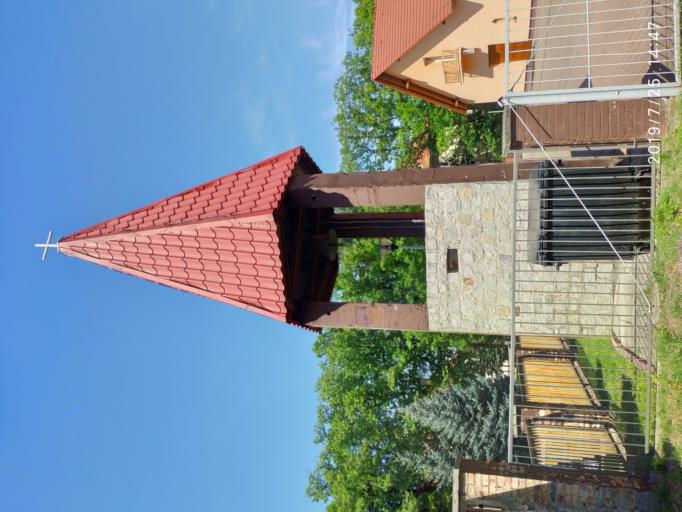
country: PL
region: Lubusz
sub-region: Powiat krosnienski
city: Krosno Odrzanskie
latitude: 52.0556
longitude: 15.1022
